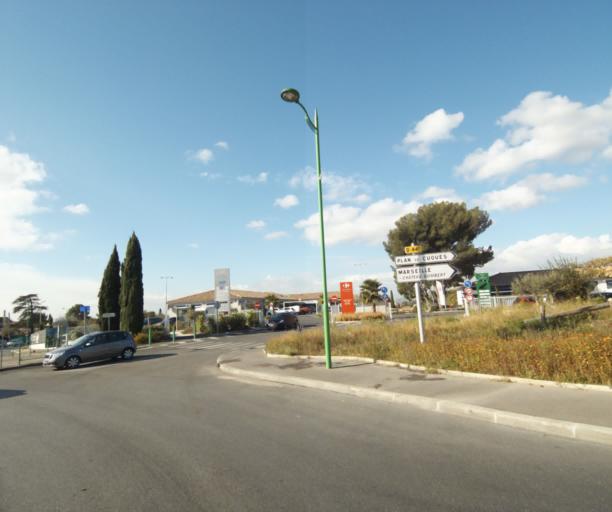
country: FR
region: Provence-Alpes-Cote d'Azur
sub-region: Departement des Bouches-du-Rhone
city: Allauch
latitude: 43.3383
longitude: 5.4742
